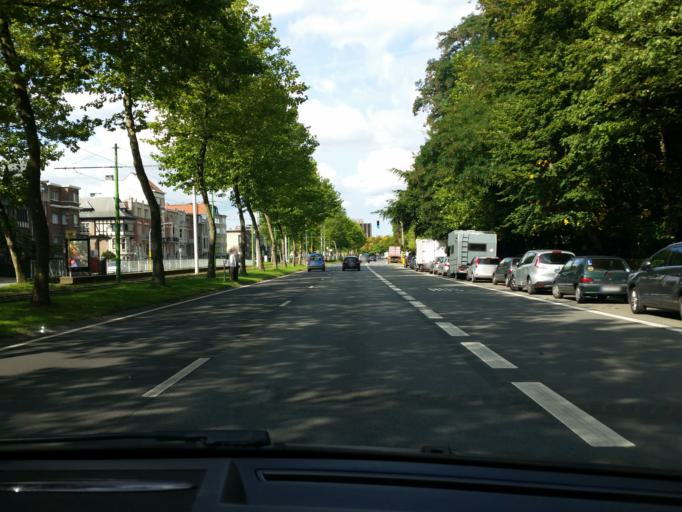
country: BE
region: Flanders
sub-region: Provincie Antwerpen
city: Mortsel
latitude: 51.1822
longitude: 4.4316
